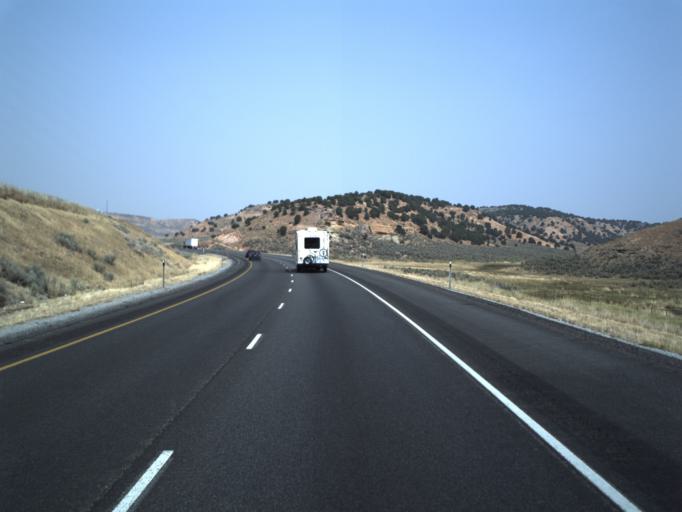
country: US
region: Wyoming
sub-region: Uinta County
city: Evanston
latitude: 41.1633
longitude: -111.1380
